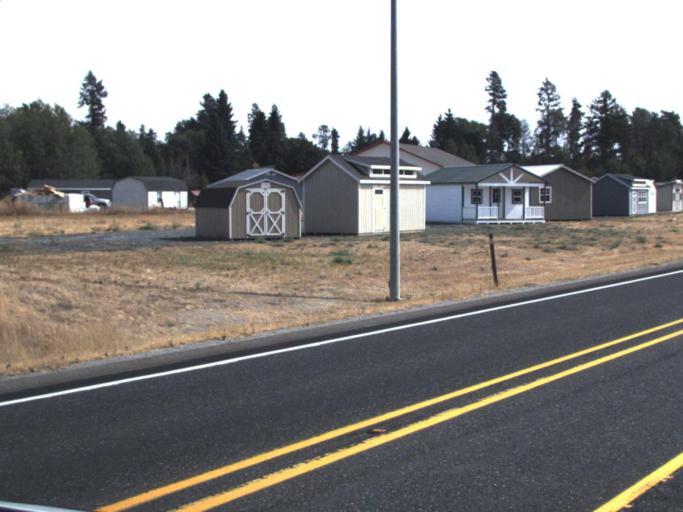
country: US
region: Washington
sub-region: Spokane County
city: Deer Park
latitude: 47.9963
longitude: -117.5717
